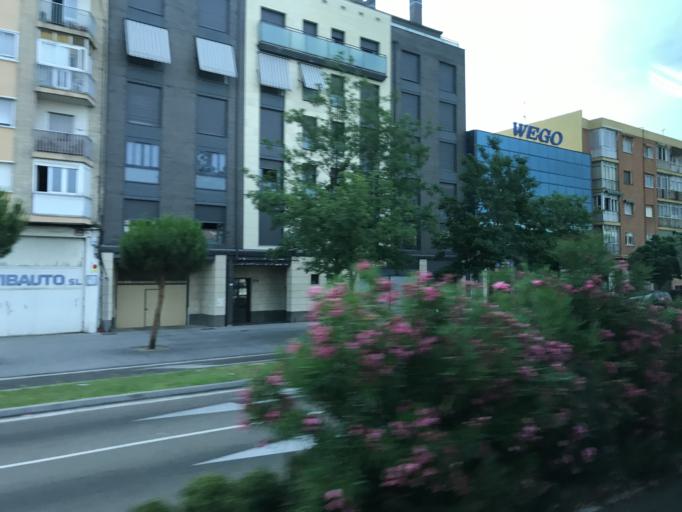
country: ES
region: Castille and Leon
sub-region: Provincia de Valladolid
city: Valladolid
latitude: 41.6288
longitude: -4.7273
